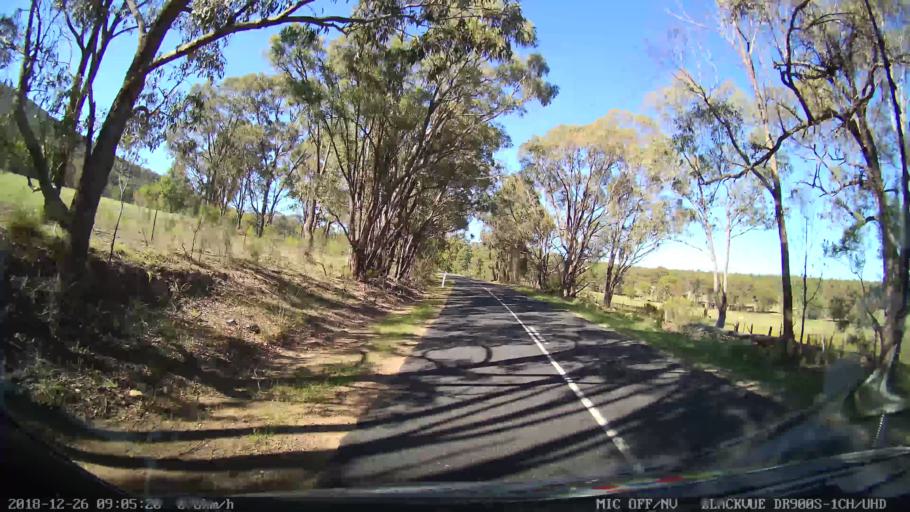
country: AU
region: New South Wales
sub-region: Mid-Western Regional
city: Kandos
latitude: -32.6817
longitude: 150.0085
